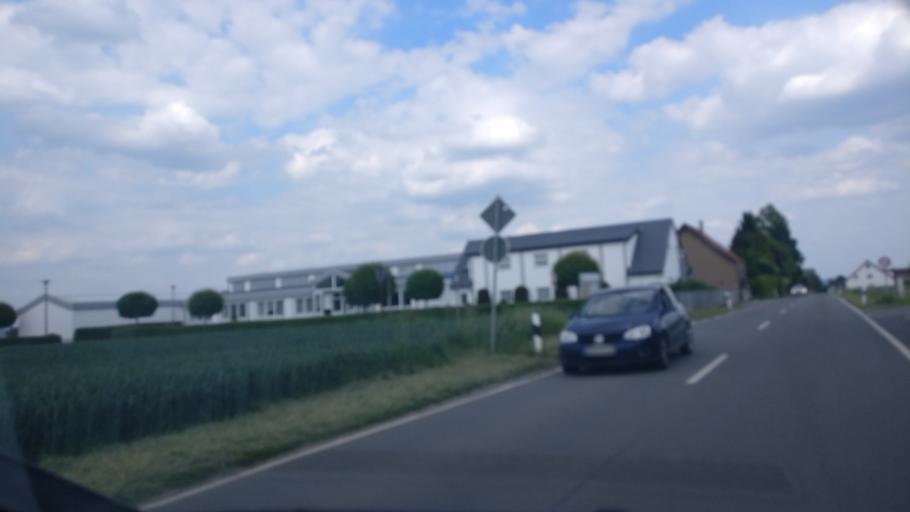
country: DE
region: North Rhine-Westphalia
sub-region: Regierungsbezirk Detmold
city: Leopoldshohe
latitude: 52.0070
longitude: 8.7096
